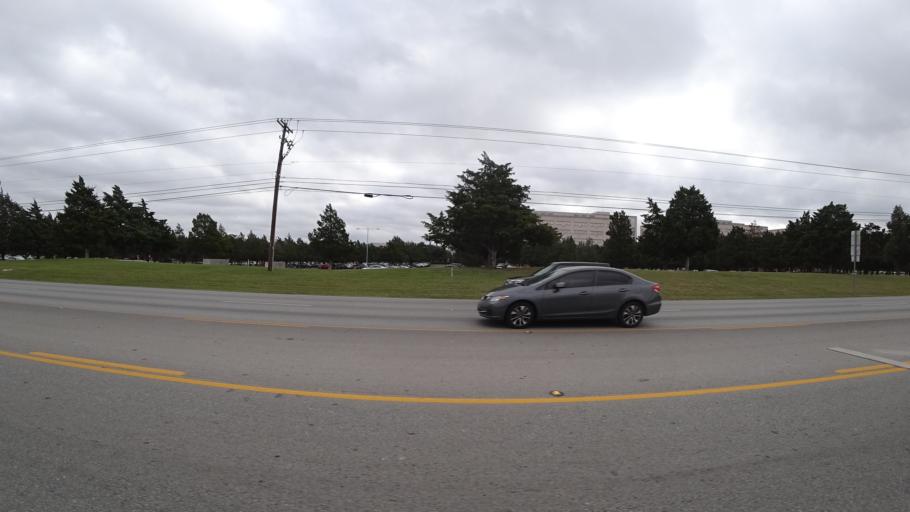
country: US
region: Texas
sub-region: Travis County
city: Wells Branch
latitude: 30.4040
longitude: -97.7167
